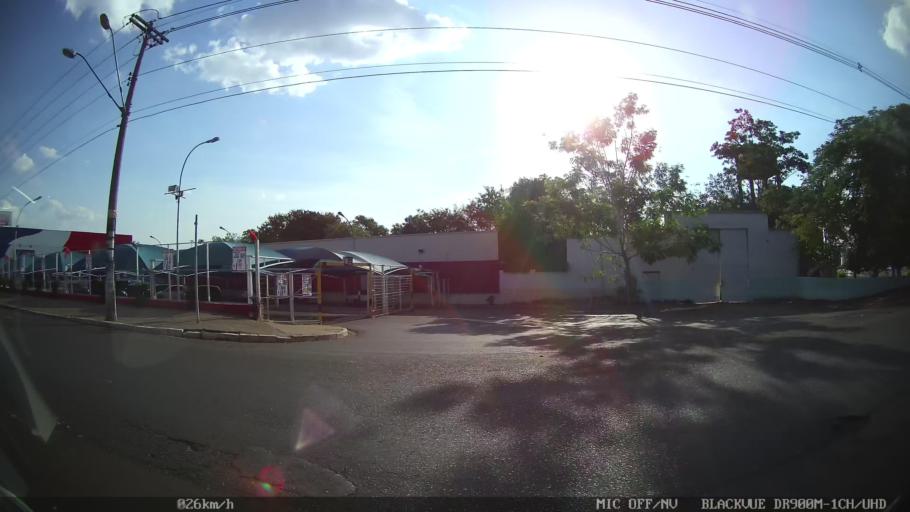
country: BR
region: Sao Paulo
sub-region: Ribeirao Preto
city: Ribeirao Preto
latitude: -21.1580
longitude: -47.8073
